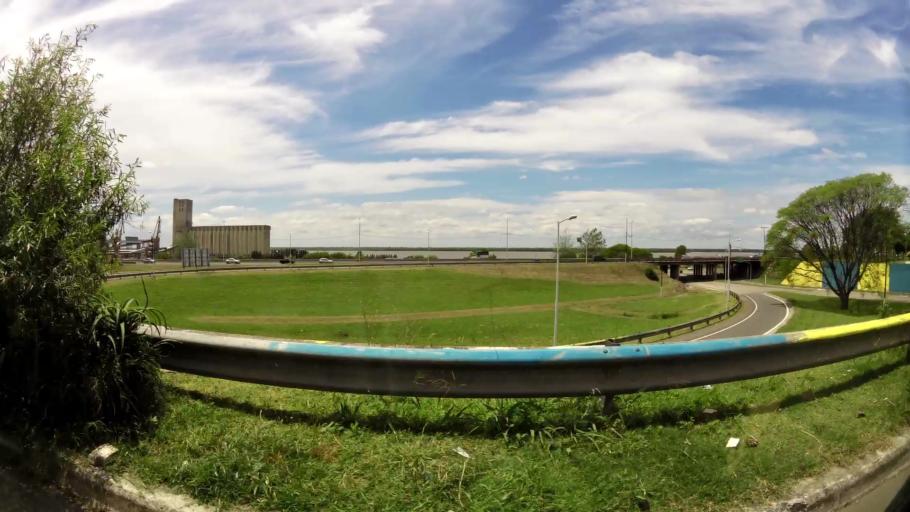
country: AR
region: Santa Fe
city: Gobernador Galvez
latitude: -32.9895
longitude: -60.6227
